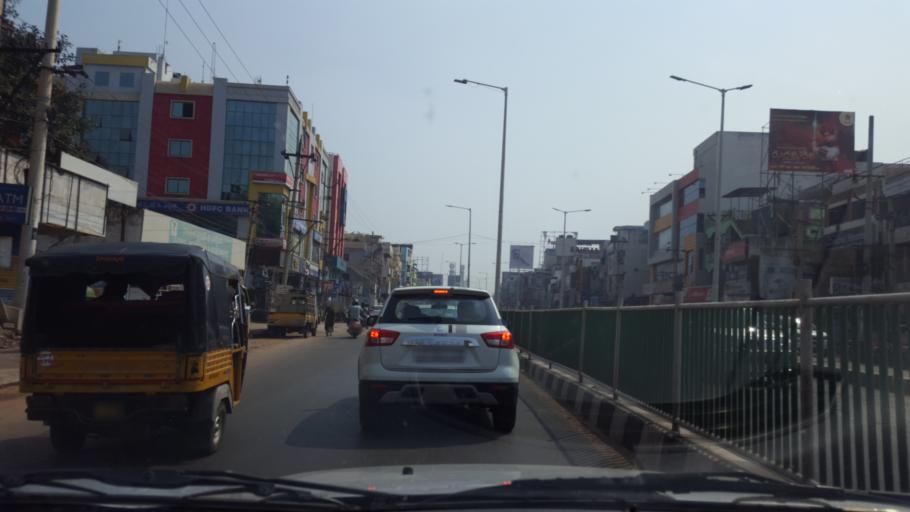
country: IN
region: Andhra Pradesh
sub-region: Vishakhapatnam
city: Vepagunta
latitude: 17.7439
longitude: 83.2301
